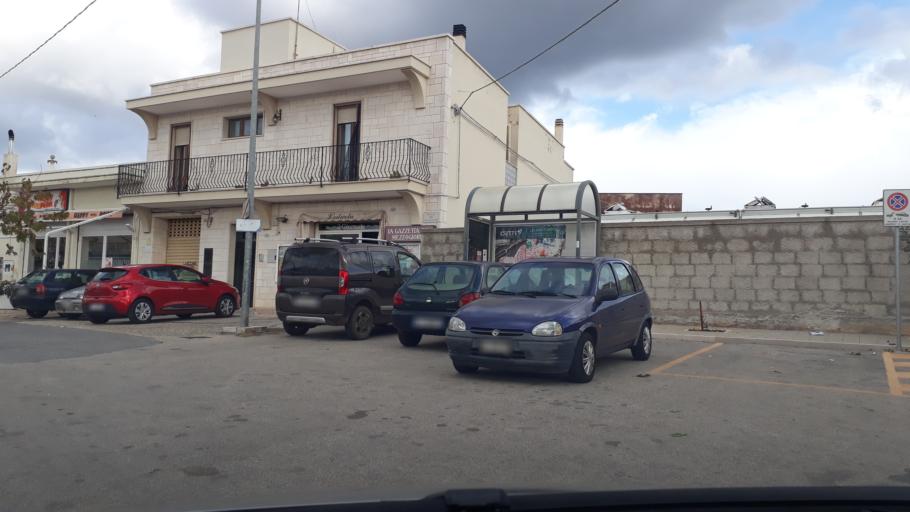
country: IT
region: Apulia
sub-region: Provincia di Brindisi
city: Cisternino
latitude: 40.7412
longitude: 17.4324
